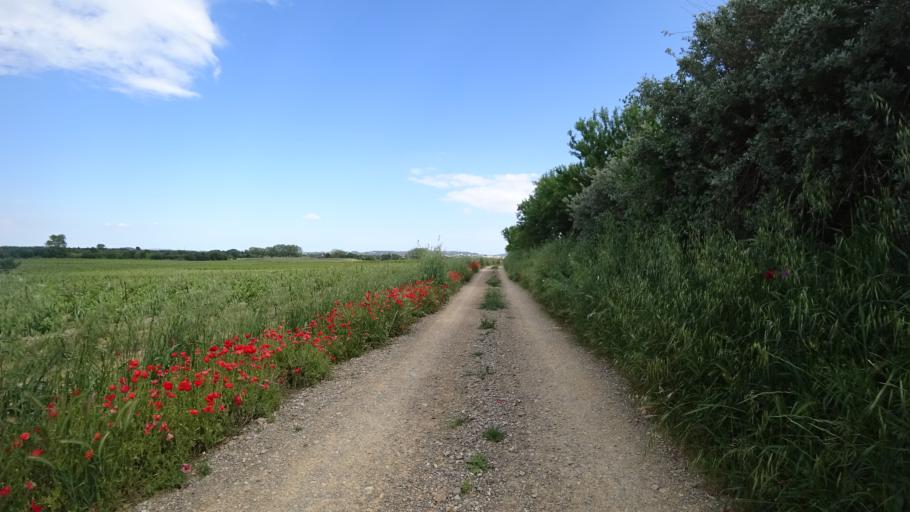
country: FR
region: Languedoc-Roussillon
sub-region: Departement de l'Aude
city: Ginestas
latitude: 43.2557
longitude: 2.8771
